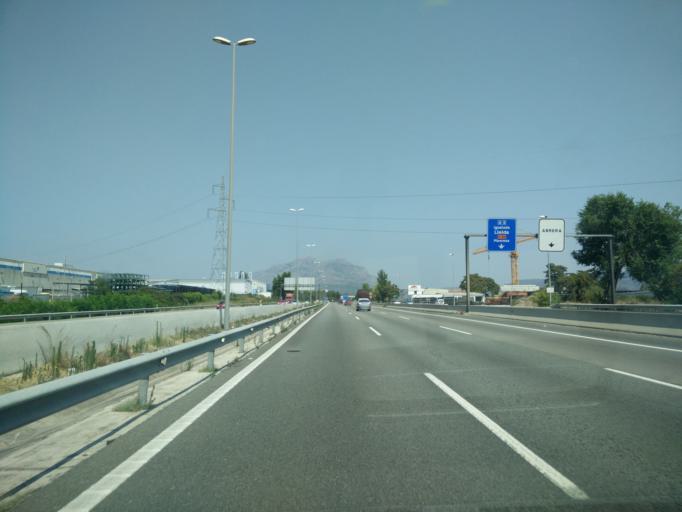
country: ES
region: Catalonia
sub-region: Provincia de Barcelona
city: Abrera
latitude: 41.5075
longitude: 1.9042
